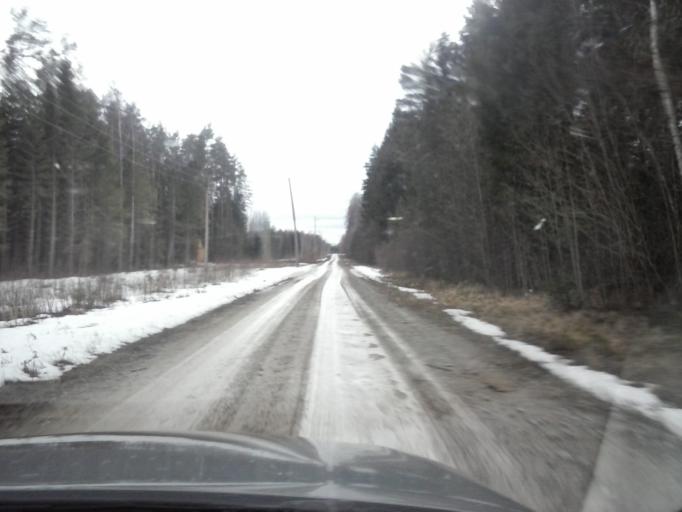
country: EE
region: Ida-Virumaa
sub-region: Johvi vald
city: Johvi
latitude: 59.1788
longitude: 27.3276
